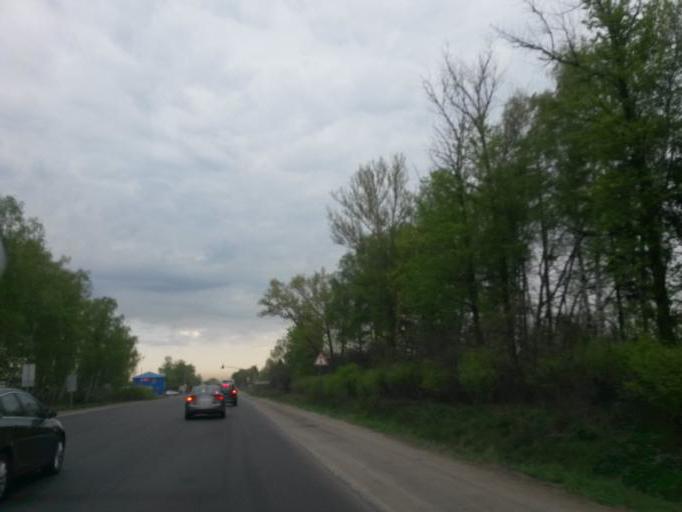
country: RU
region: Moskovskaya
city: Belyye Stolby
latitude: 55.3024
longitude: 37.8158
